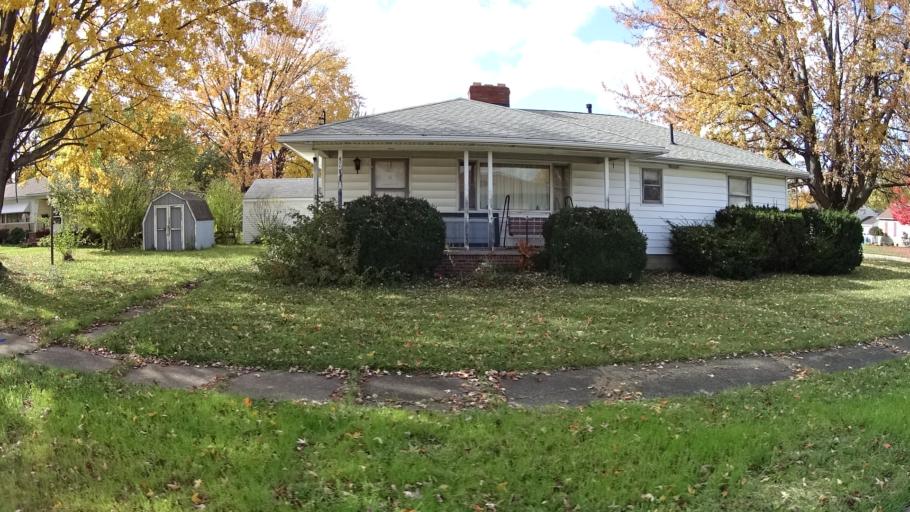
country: US
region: Ohio
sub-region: Lorain County
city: Lorain
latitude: 41.4385
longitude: -82.1868
